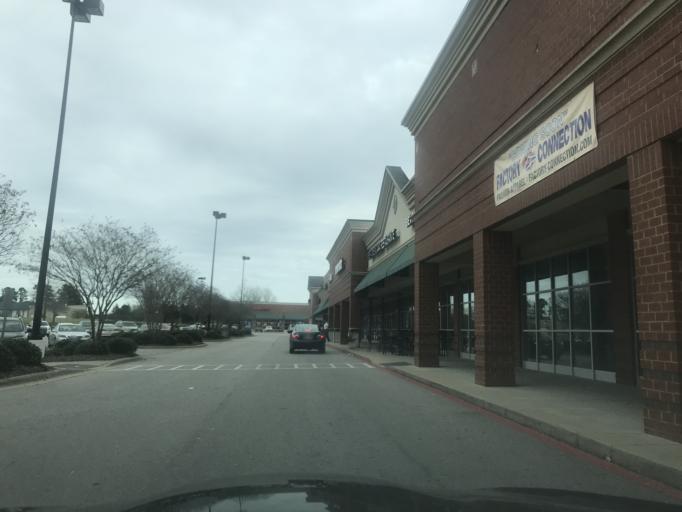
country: US
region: North Carolina
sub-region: Franklin County
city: Louisburg
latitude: 36.0830
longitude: -78.3190
